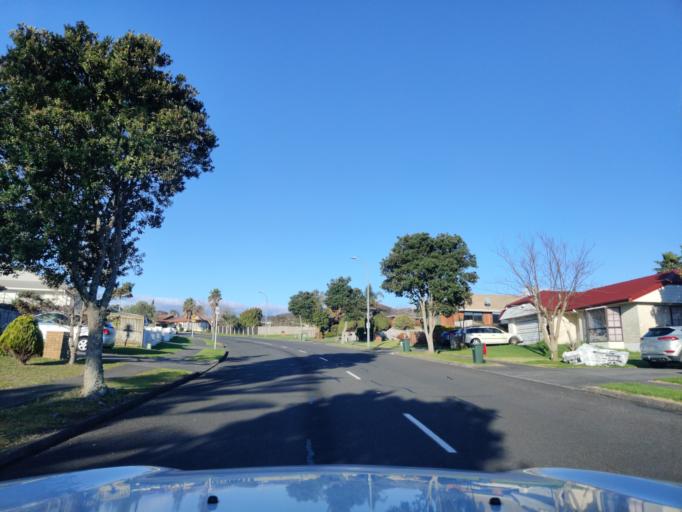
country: NZ
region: Auckland
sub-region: Auckland
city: Pakuranga
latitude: -36.9180
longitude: 174.9214
